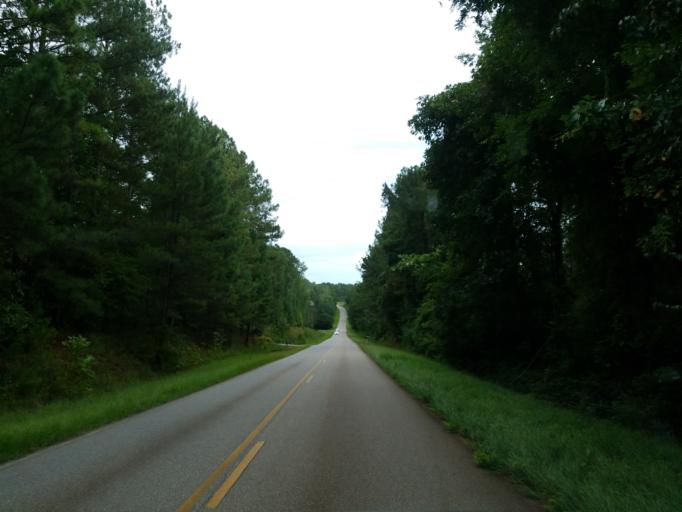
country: US
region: Georgia
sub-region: Bibb County
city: West Point
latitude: 32.8995
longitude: -83.8422
